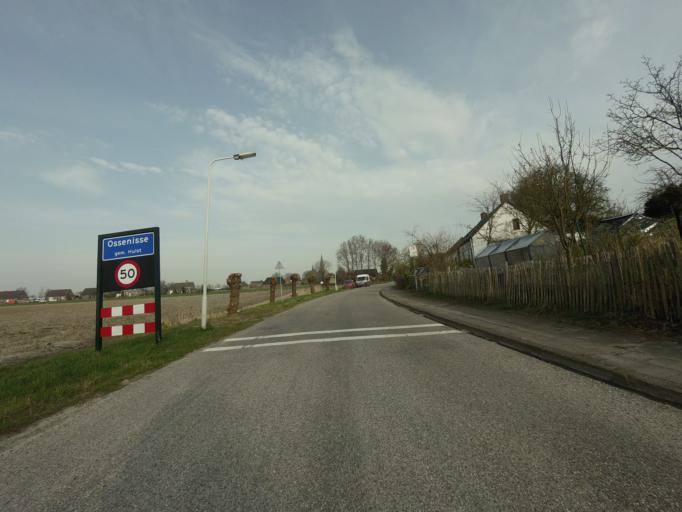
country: NL
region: Zeeland
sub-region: Gemeente Terneuzen
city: Zaamslag
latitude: 51.3891
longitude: 3.9752
